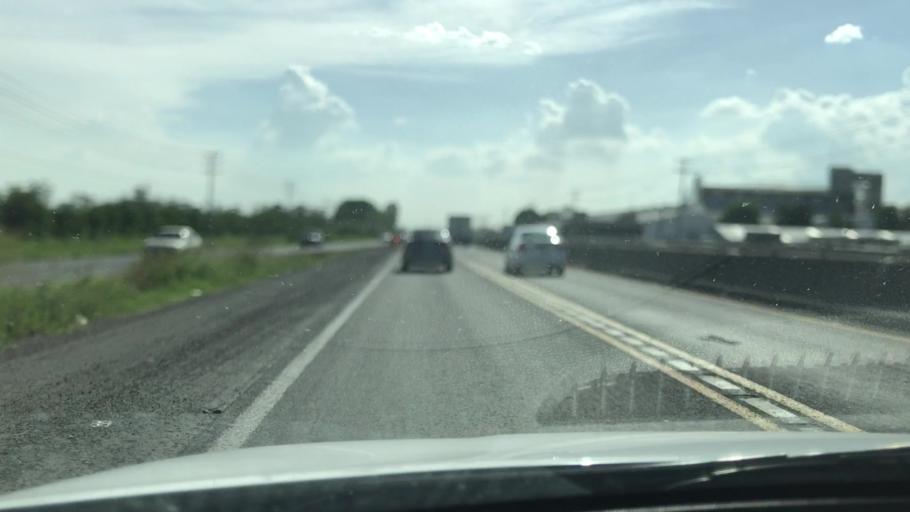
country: MX
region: Guanajuato
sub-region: Celaya
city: Colonia Fraccionamiento el Puente
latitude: 20.5145
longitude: -100.9055
